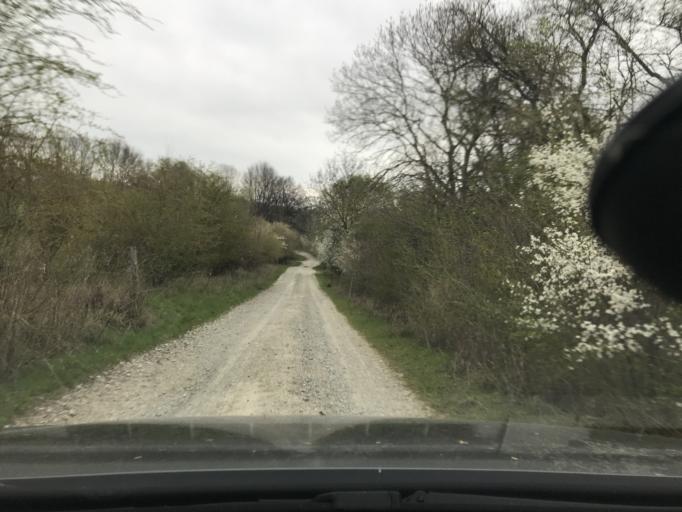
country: DE
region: Thuringia
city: Muehlhausen
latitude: 51.2210
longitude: 10.4249
